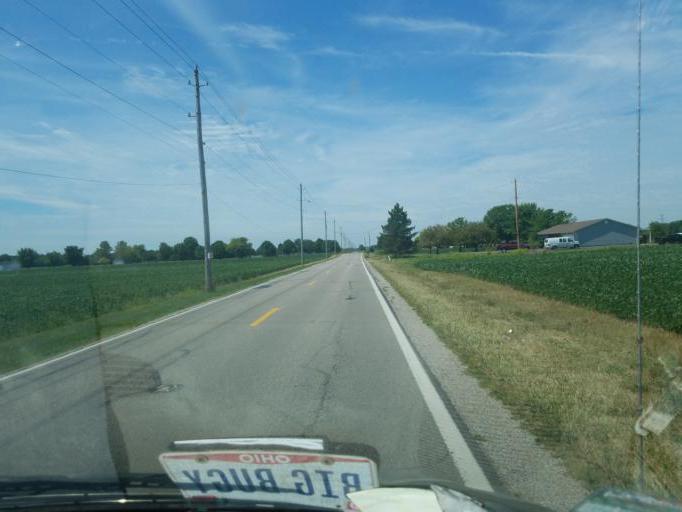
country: US
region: Ohio
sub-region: Franklin County
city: Grove City
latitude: 39.8602
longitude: -83.1284
